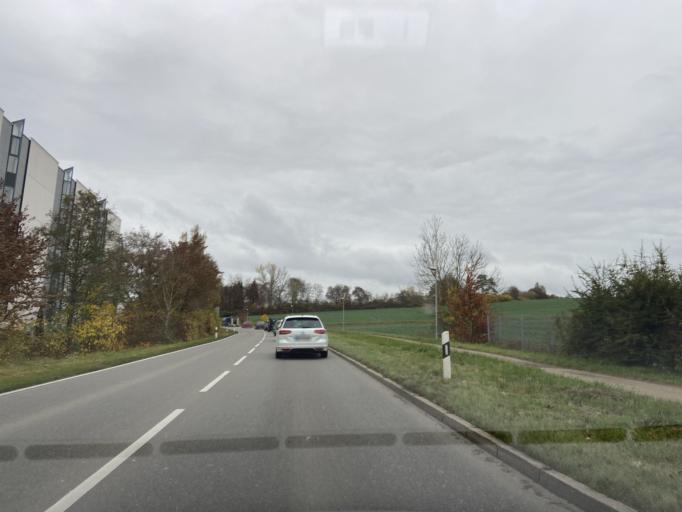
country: DE
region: Baden-Wuerttemberg
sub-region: Tuebingen Region
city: Sigmaringen
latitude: 48.0813
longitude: 9.2321
